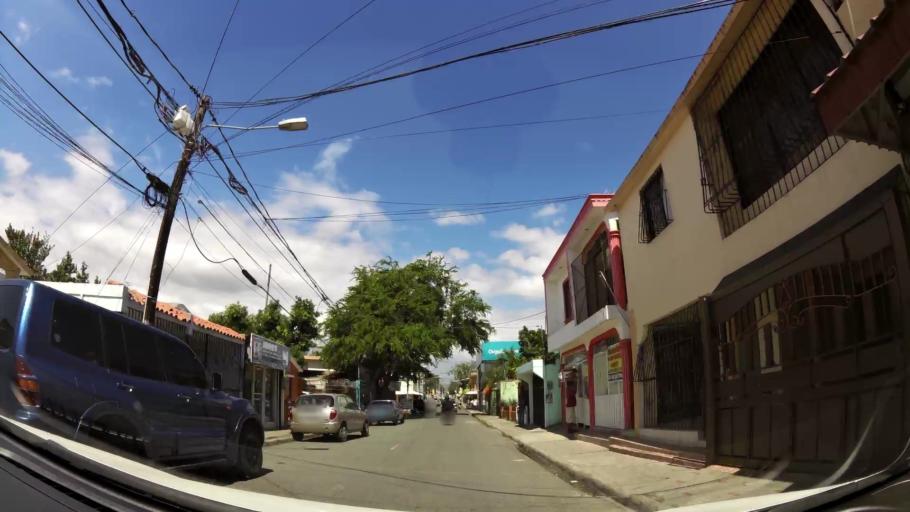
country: DO
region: San Cristobal
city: San Cristobal
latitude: 18.4110
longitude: -70.1079
